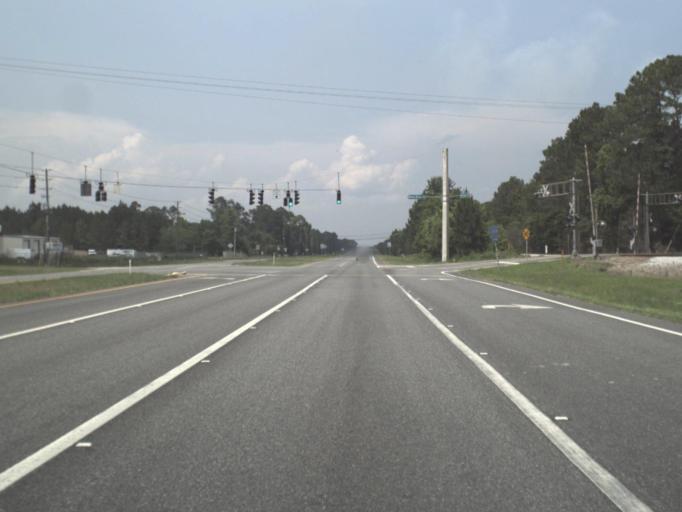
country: US
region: Florida
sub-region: Putnam County
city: Palatka
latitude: 29.7150
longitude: -81.6581
